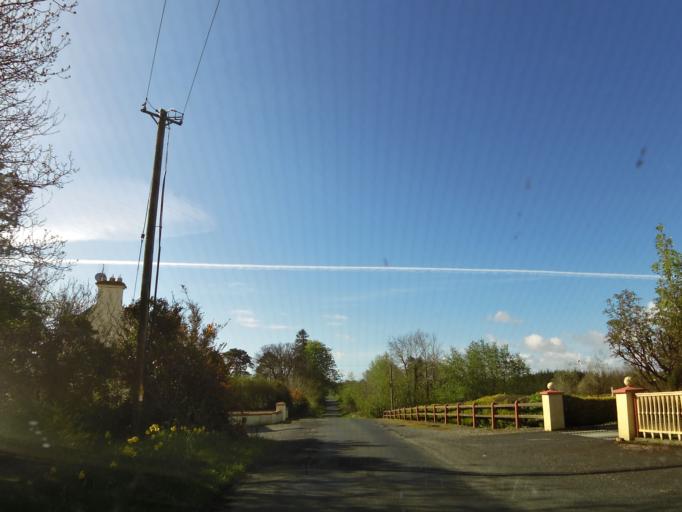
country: IE
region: Connaught
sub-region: Maigh Eo
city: Claremorris
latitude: 53.7818
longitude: -8.9608
